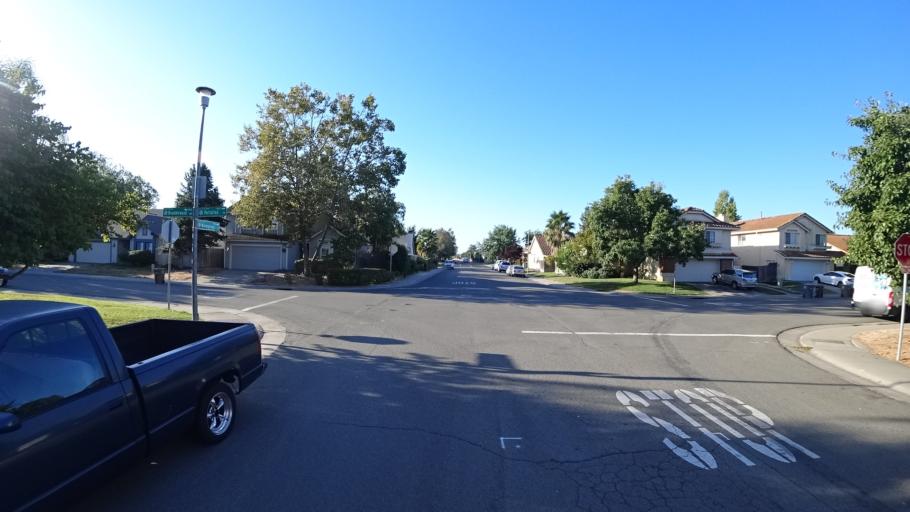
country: US
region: California
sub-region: Sacramento County
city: Laguna
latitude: 38.4318
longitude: -121.4544
